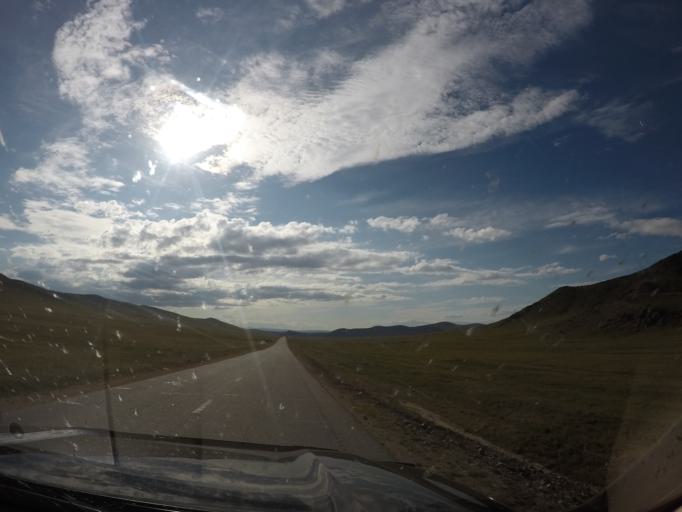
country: MN
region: Central Aimak
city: Bayandelger
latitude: 47.6937
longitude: 108.5237
